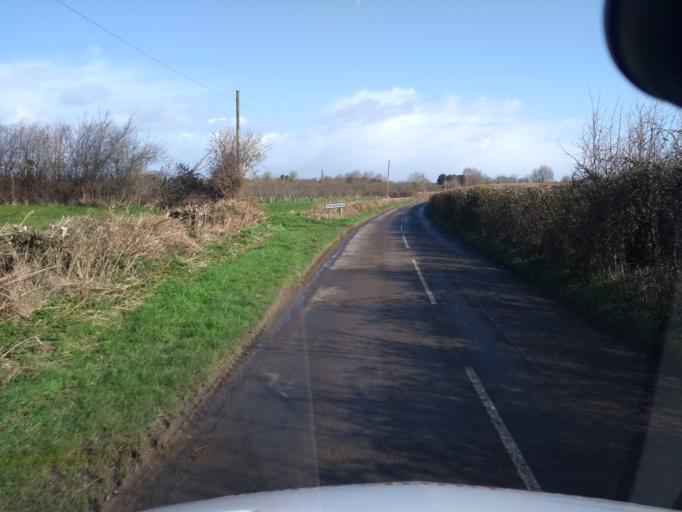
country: GB
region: England
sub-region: Somerset
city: South Petherton
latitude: 50.9736
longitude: -2.8255
